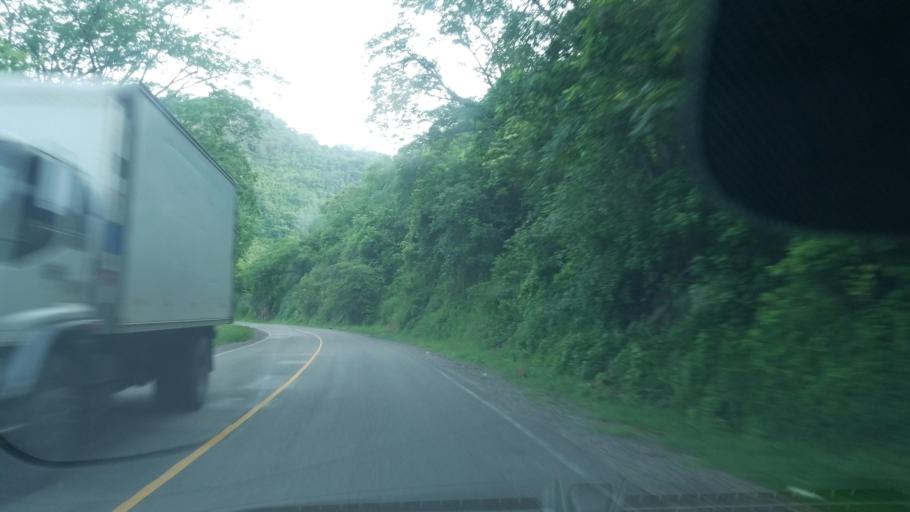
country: HN
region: Santa Barbara
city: Trinidad
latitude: 15.1126
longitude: -88.2053
